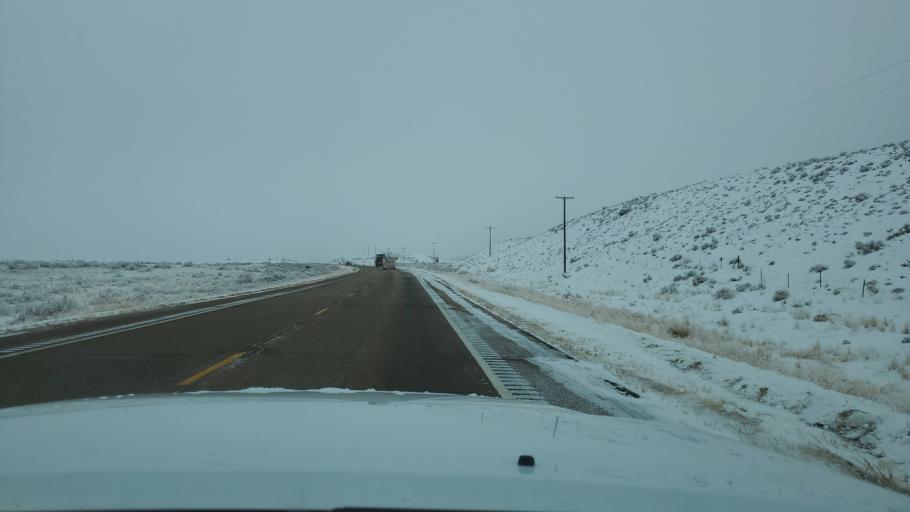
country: US
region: Colorado
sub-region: Rio Blanco County
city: Rangely
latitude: 40.2426
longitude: -108.9491
